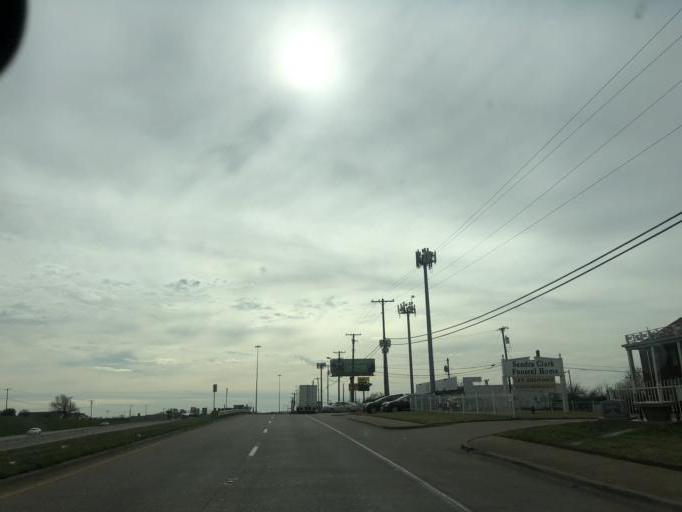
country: US
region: Texas
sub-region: Dallas County
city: Duncanville
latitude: 32.6743
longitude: -96.8230
